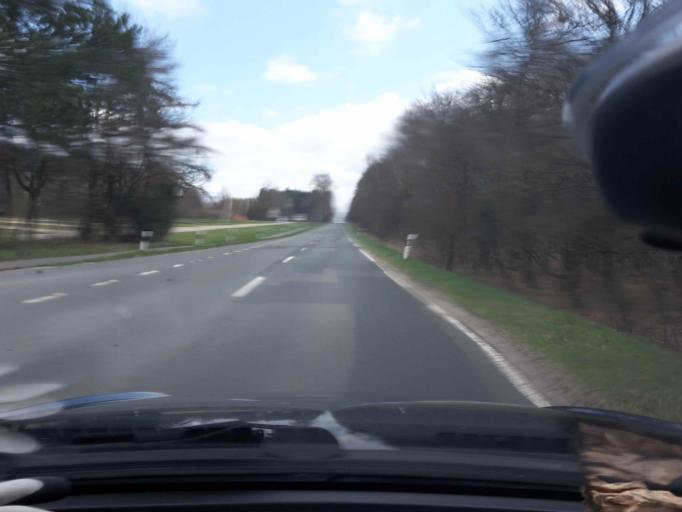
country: DE
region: Lower Saxony
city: Hanstedt
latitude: 53.2357
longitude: 10.0450
